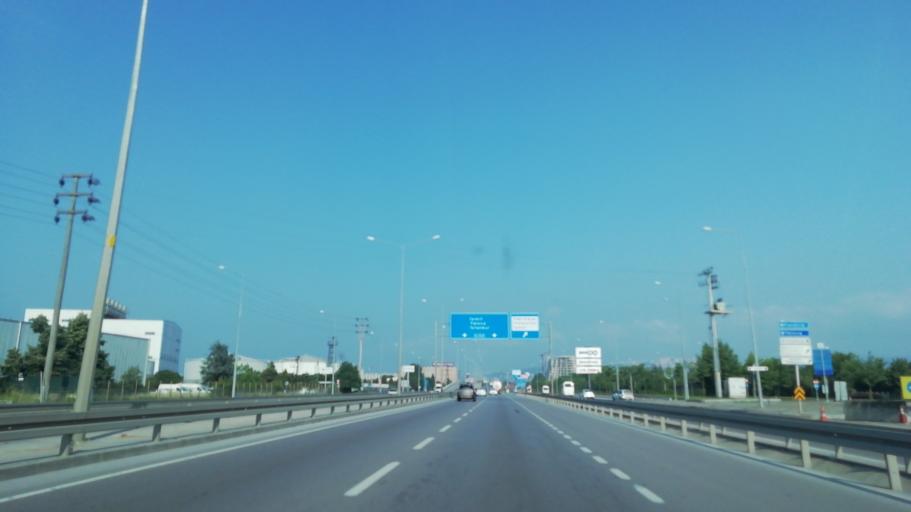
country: TR
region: Kocaeli
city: Kosekoy
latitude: 40.7577
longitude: 29.9945
